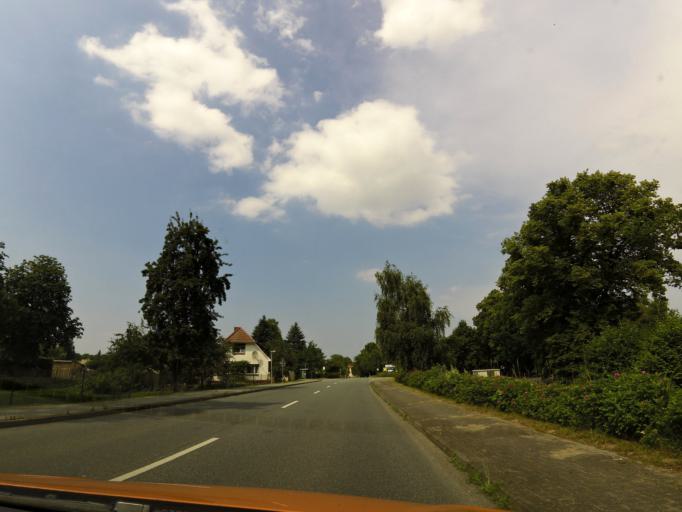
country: DE
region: Mecklenburg-Vorpommern
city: Krakow am See
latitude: 53.6843
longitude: 12.2679
